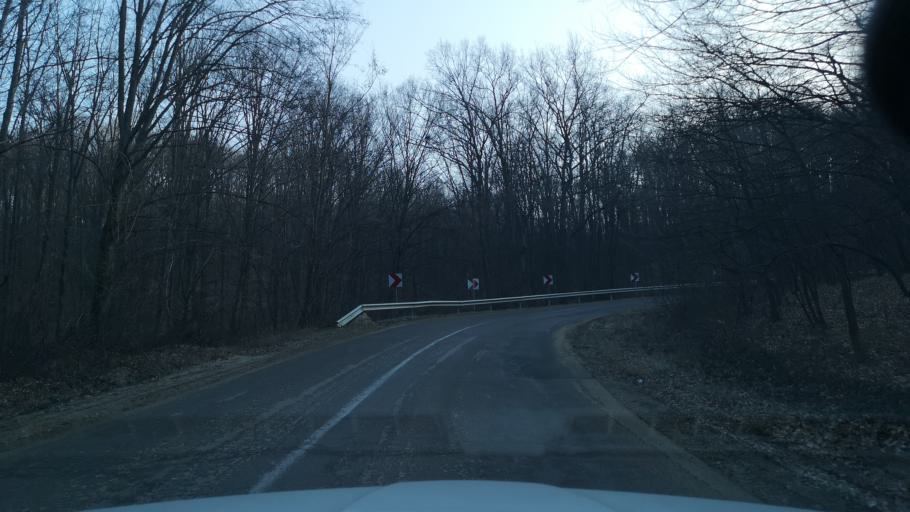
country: MD
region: Stinga Nistrului
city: Bucovat
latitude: 47.1393
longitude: 28.4994
